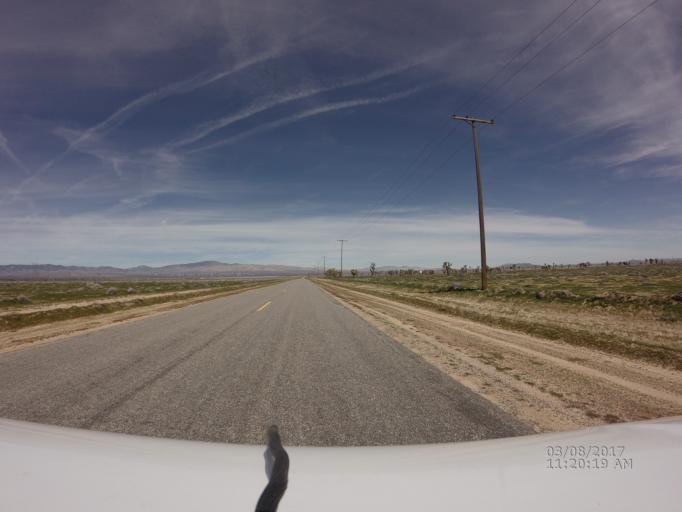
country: US
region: California
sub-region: Los Angeles County
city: Green Valley
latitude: 34.7838
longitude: -118.3789
